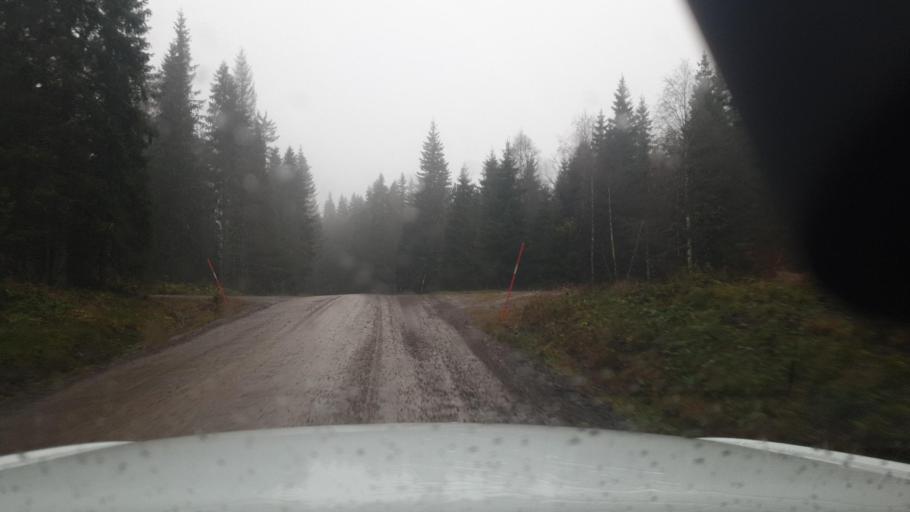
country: SE
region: Vaermland
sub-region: Sunne Kommun
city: Sunne
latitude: 59.8267
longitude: 12.8961
